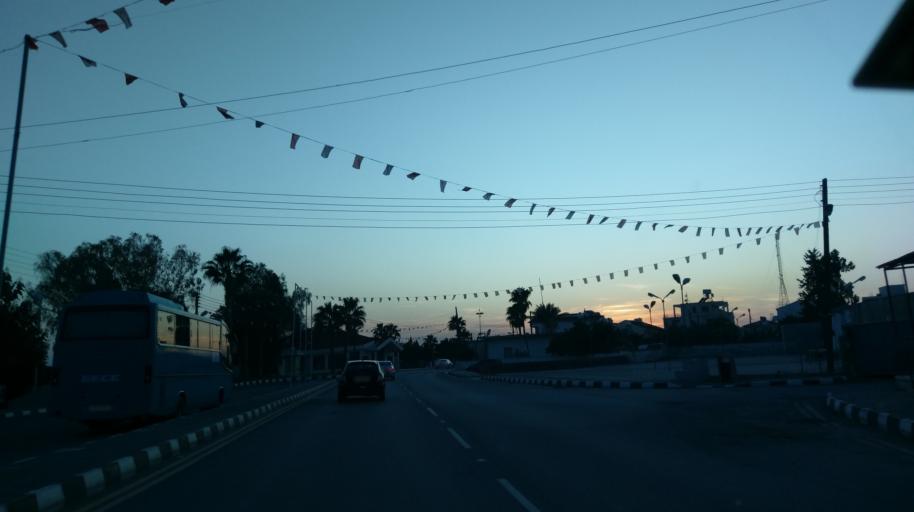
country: CY
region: Ammochostos
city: Trikomo
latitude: 35.2846
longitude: 33.8950
